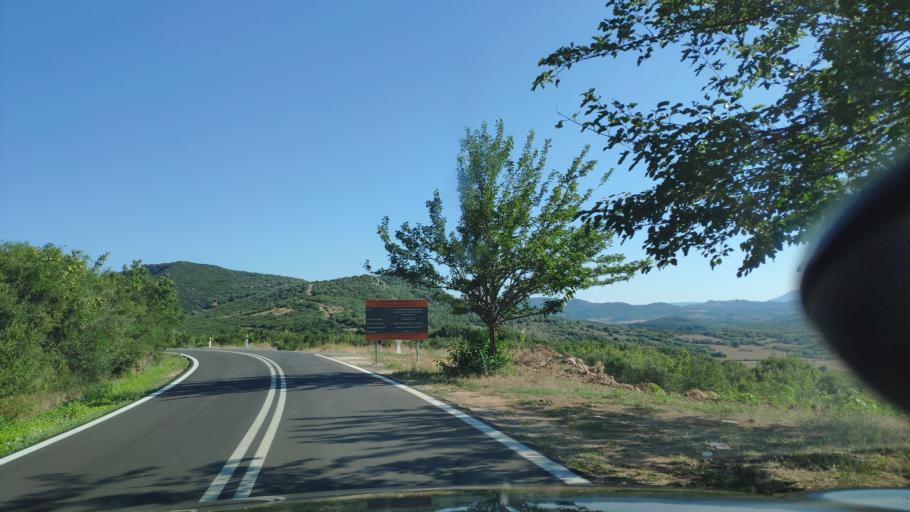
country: GR
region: West Greece
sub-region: Nomos Aitolias kai Akarnanias
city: Fitiai
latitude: 38.6657
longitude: 21.1439
